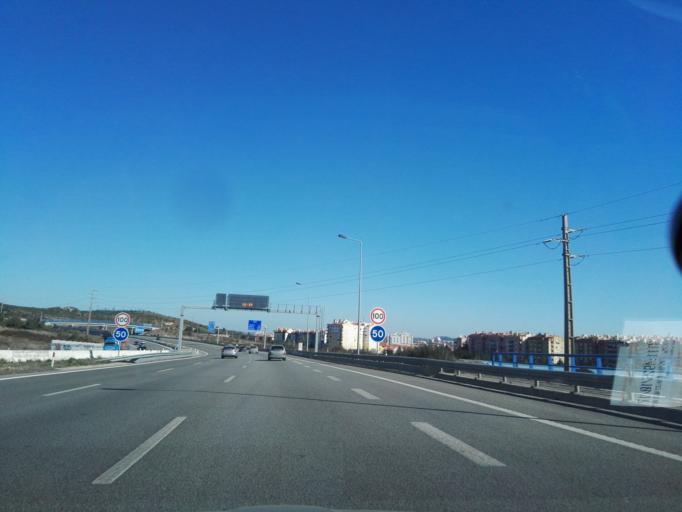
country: PT
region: Lisbon
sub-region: Sintra
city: Sintra
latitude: 38.7858
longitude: -9.3600
